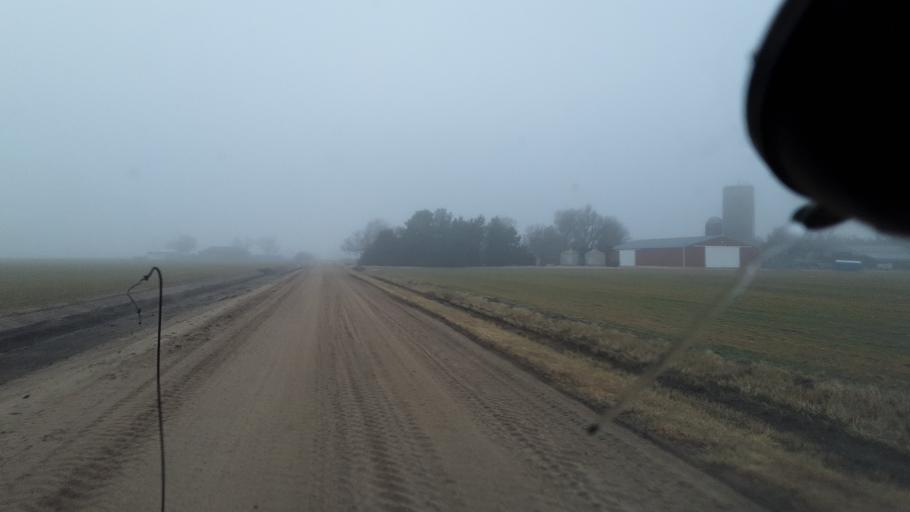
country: US
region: Kansas
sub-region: Reno County
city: South Hutchinson
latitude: 37.9843
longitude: -97.9876
